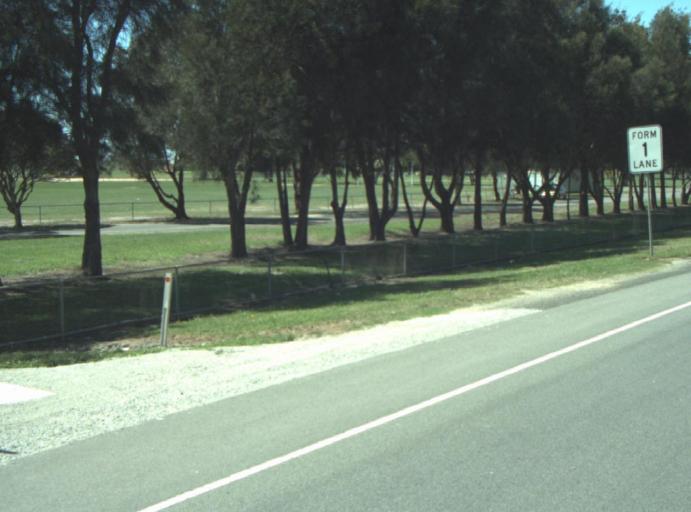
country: AU
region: Victoria
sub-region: Greater Geelong
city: Breakwater
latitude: -38.1816
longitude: 144.3542
